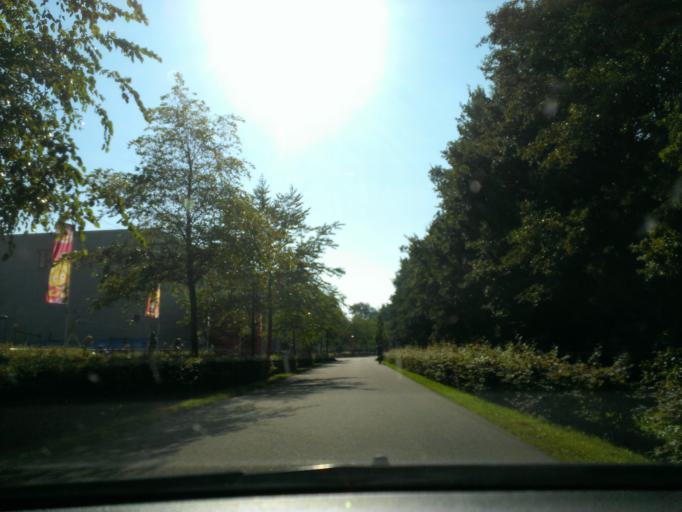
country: NL
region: Drenthe
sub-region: Gemeente Coevorden
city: Dalen
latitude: 52.6789
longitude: 6.7722
